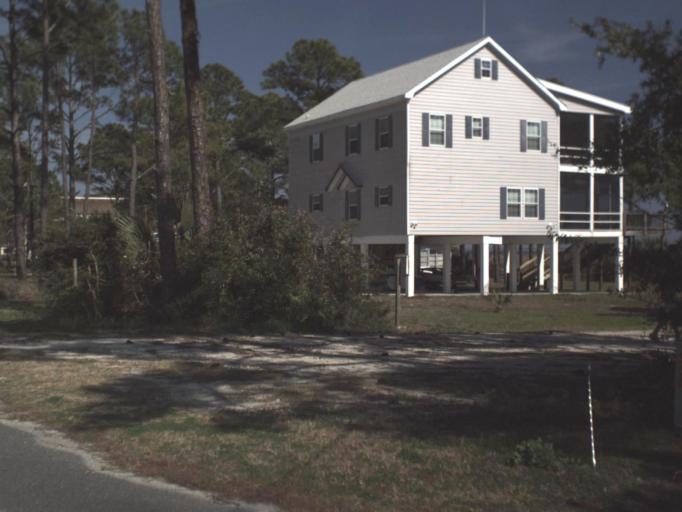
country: US
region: Florida
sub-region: Franklin County
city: Carrabelle
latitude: 29.8312
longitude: -84.6895
